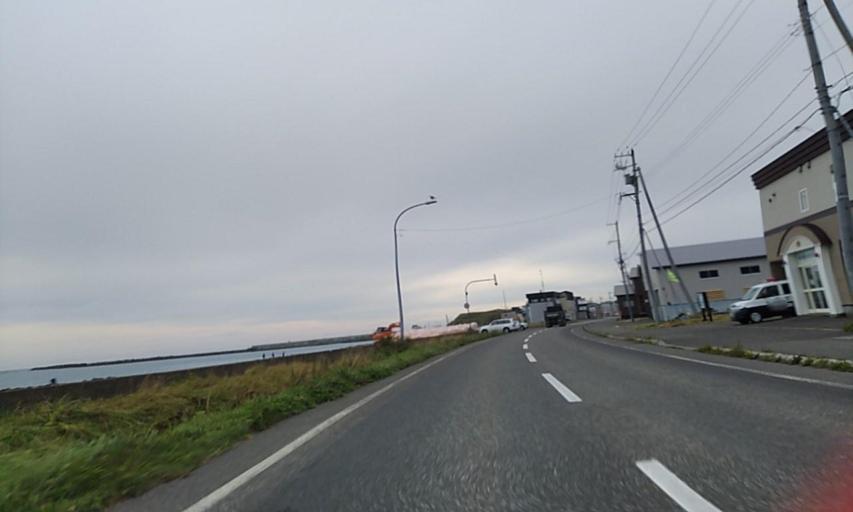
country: JP
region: Hokkaido
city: Makubetsu
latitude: 45.3832
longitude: 142.0848
